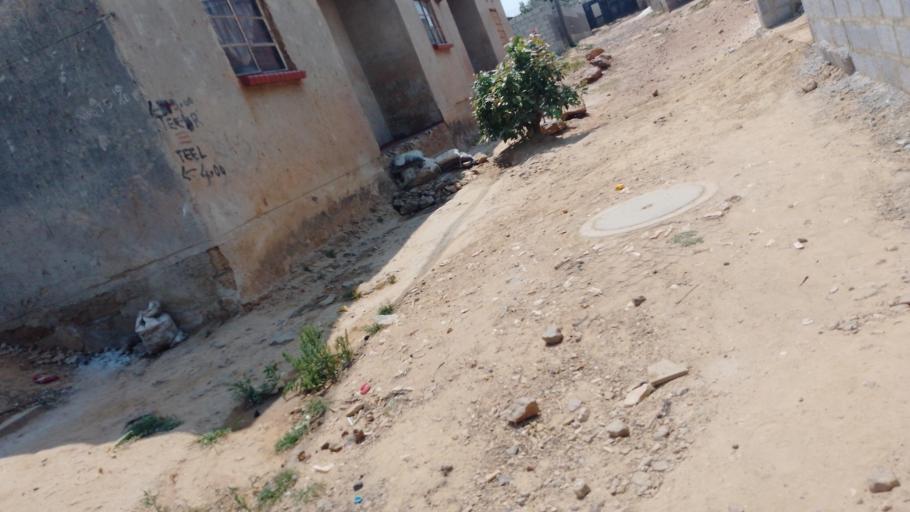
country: ZM
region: Lusaka
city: Lusaka
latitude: -15.3986
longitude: 28.3667
